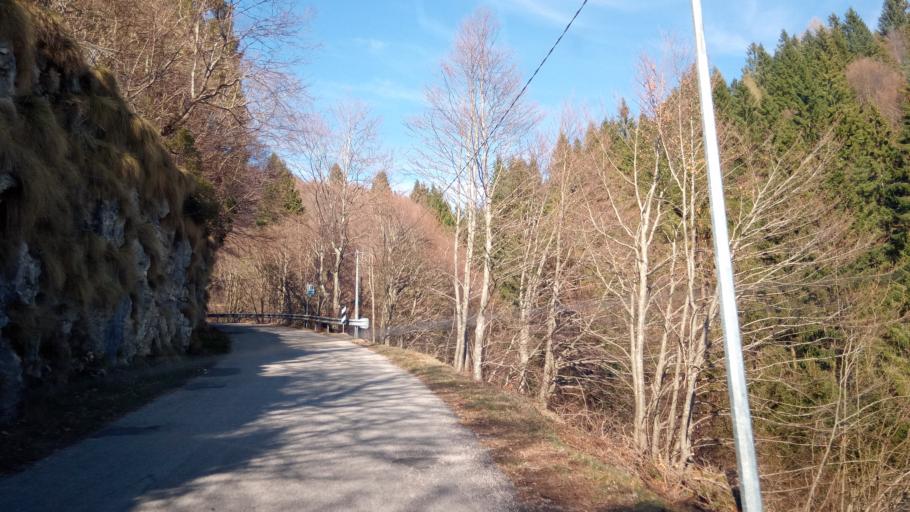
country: IT
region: Veneto
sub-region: Provincia di Treviso
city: Borso del Grappa
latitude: 45.8397
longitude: 11.7808
